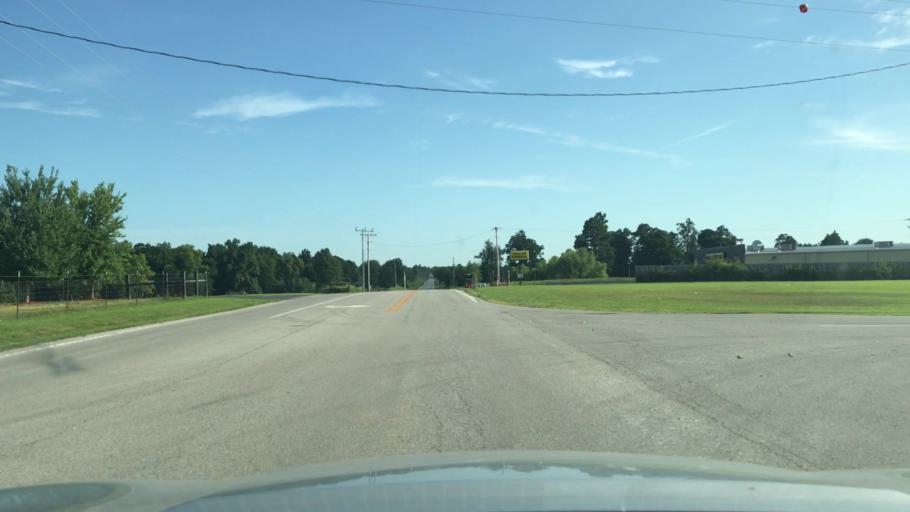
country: US
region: Kentucky
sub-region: Todd County
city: Elkton
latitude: 36.9130
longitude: -87.1632
